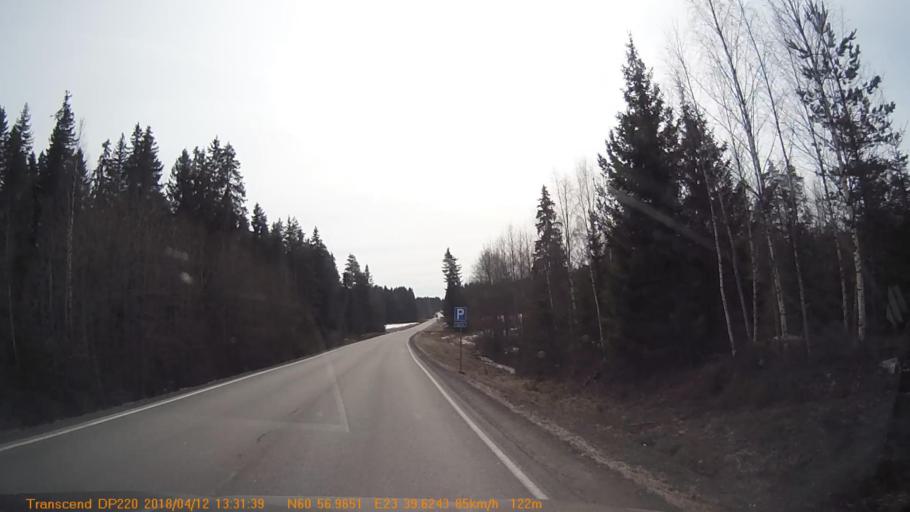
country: FI
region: Haeme
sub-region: Forssa
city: Forssa
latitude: 60.9494
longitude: 23.6604
